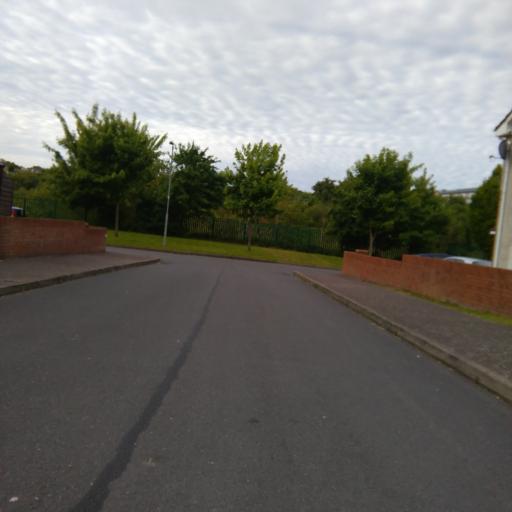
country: IE
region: Munster
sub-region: County Cork
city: Cork
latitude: 51.9142
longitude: -8.4560
